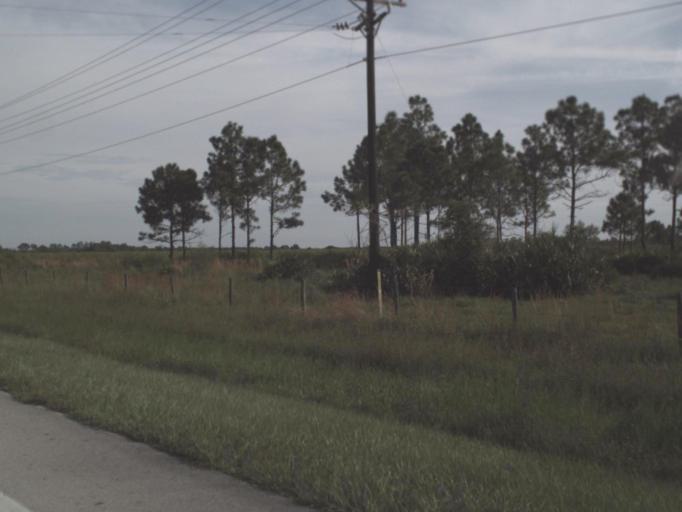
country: US
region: Florida
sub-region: Lee County
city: Fort Myers Shores
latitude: 26.7445
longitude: -81.7609
